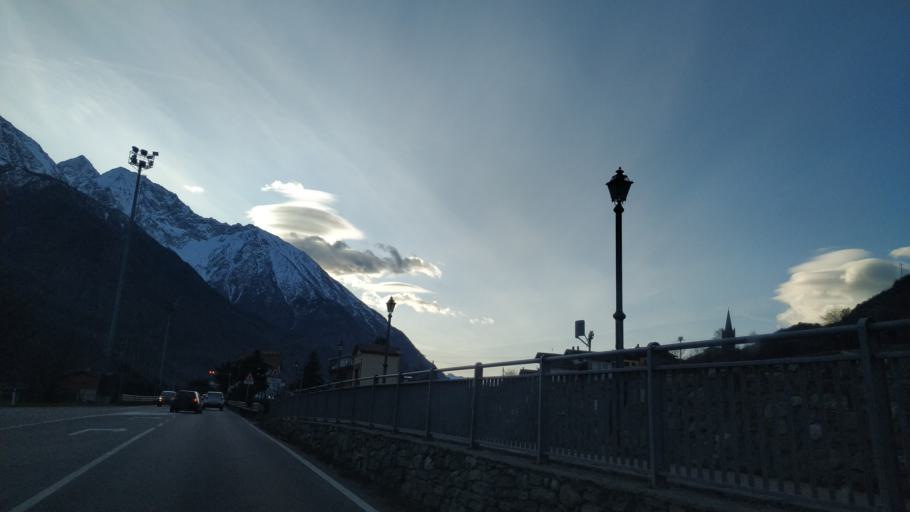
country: IT
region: Aosta Valley
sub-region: Valle d'Aosta
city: Nus
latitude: 45.7418
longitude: 7.4754
